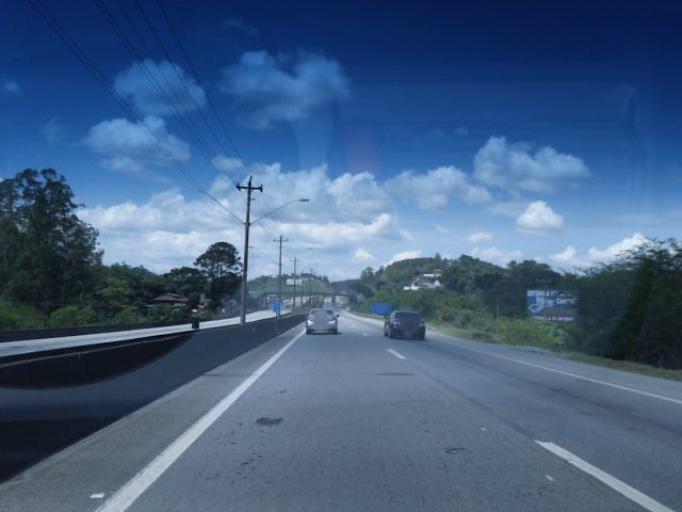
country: BR
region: Sao Paulo
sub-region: Sao Lourenco Da Serra
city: Sao Lourenco da Serra
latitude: -23.8932
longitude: -46.9843
